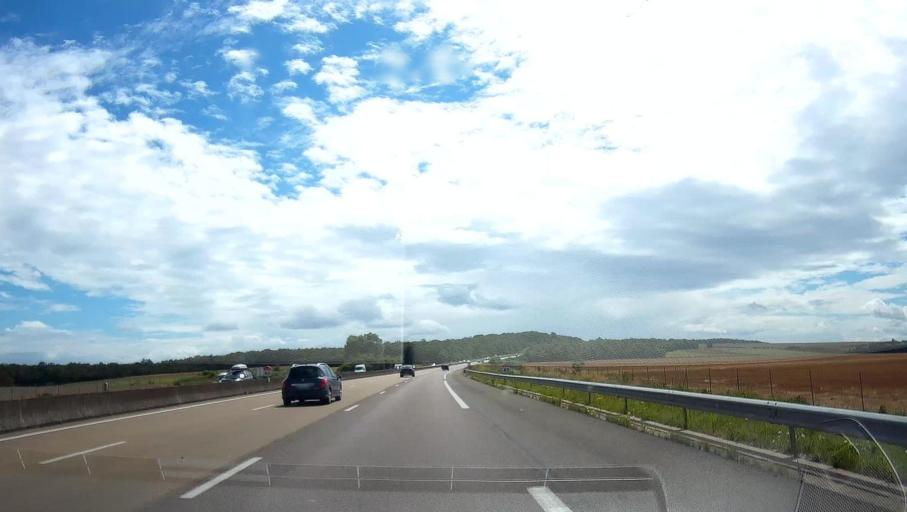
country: FR
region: Bourgogne
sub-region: Departement de la Cote-d'Or
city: Marcilly-sur-Tille
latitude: 47.4776
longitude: 5.1893
